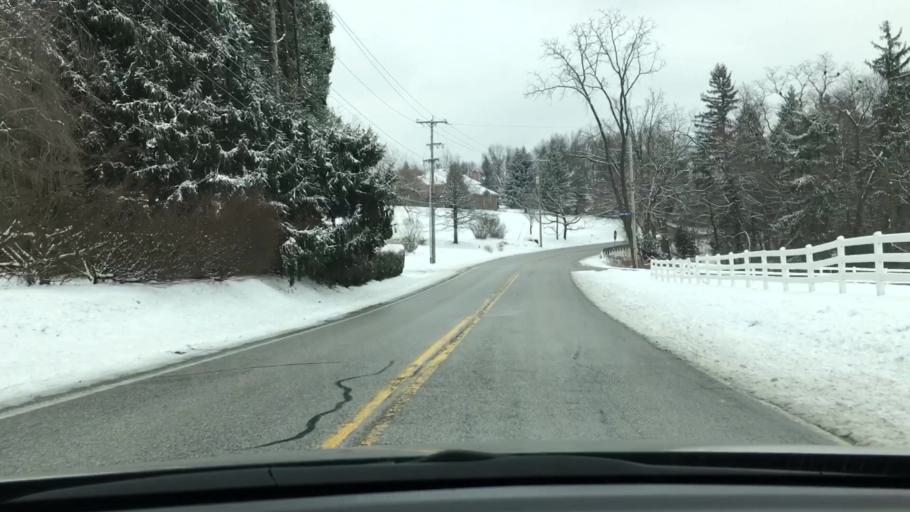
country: US
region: Pennsylvania
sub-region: York County
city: Grantley
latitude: 39.9328
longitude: -76.7264
